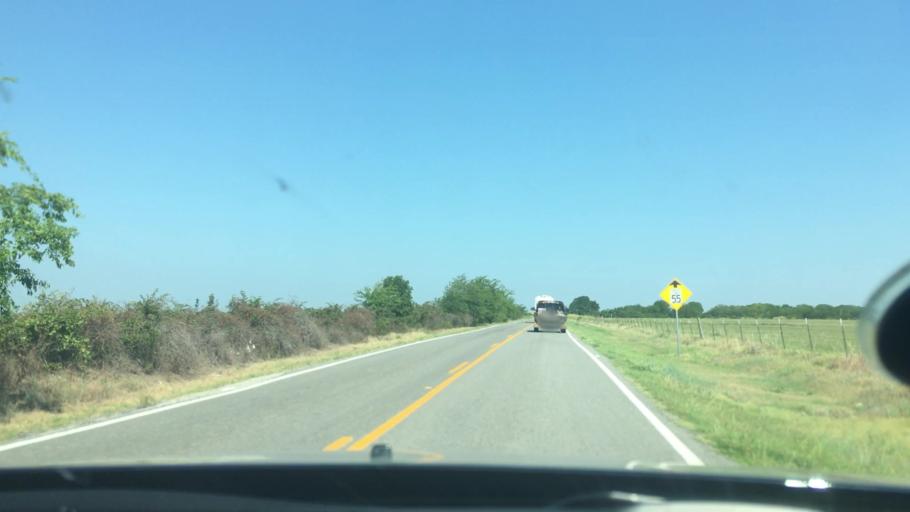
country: US
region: Oklahoma
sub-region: Johnston County
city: Tishomingo
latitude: 34.1964
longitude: -96.5390
